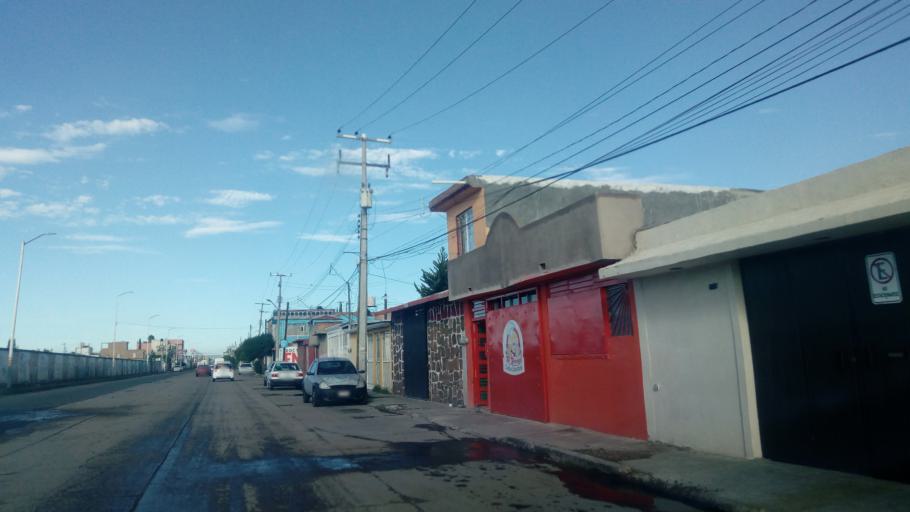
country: MX
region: Durango
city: Victoria de Durango
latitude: 24.0551
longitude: -104.6041
